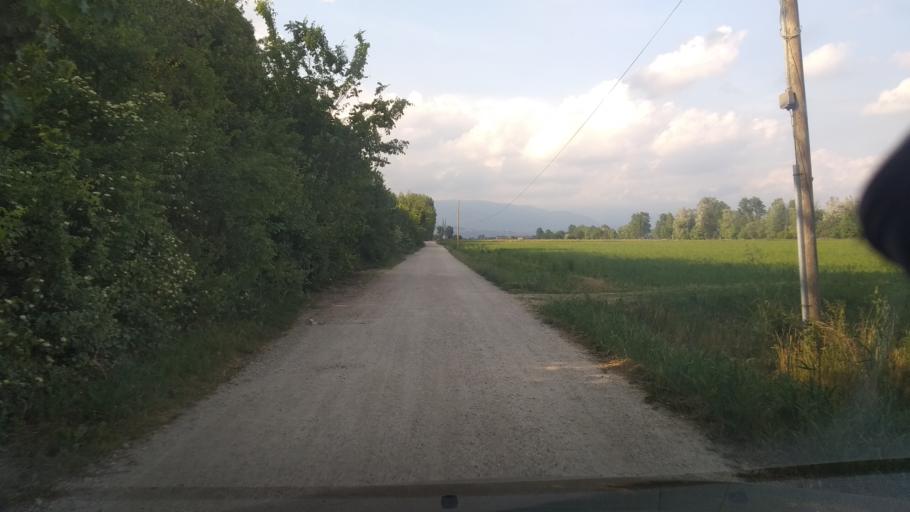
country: IT
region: Veneto
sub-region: Provincia di Vicenza
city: Sandrigo
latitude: 45.6675
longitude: 11.6106
